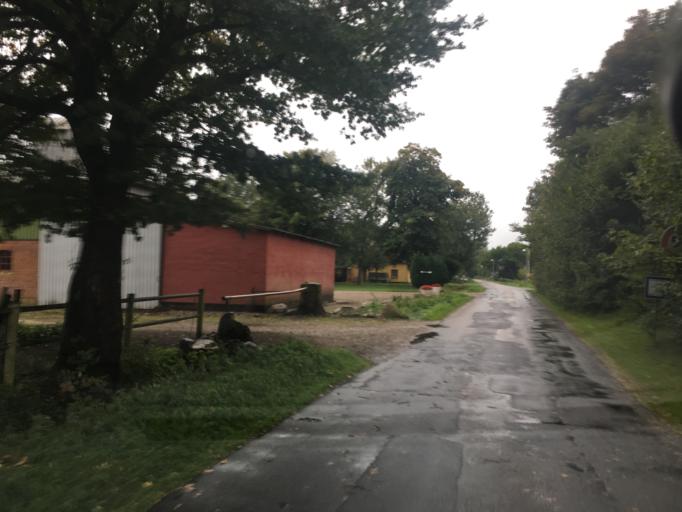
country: DE
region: Schleswig-Holstein
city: Bramstedtlund
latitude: 54.9575
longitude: 9.0533
